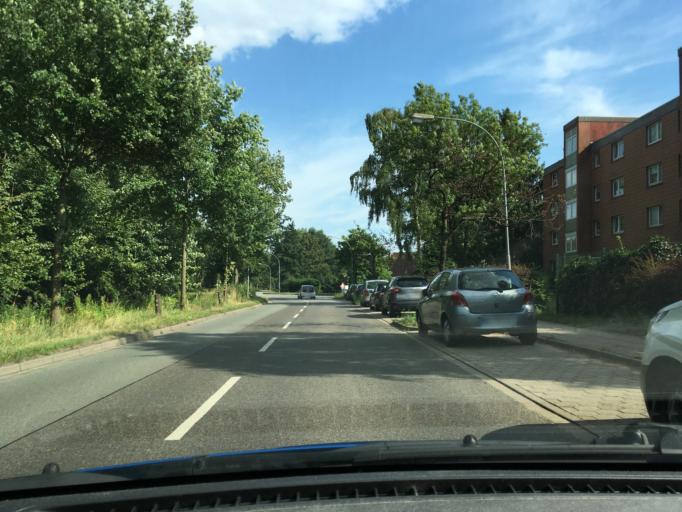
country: DE
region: Lower Saxony
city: Stelle
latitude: 53.4040
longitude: 10.0502
